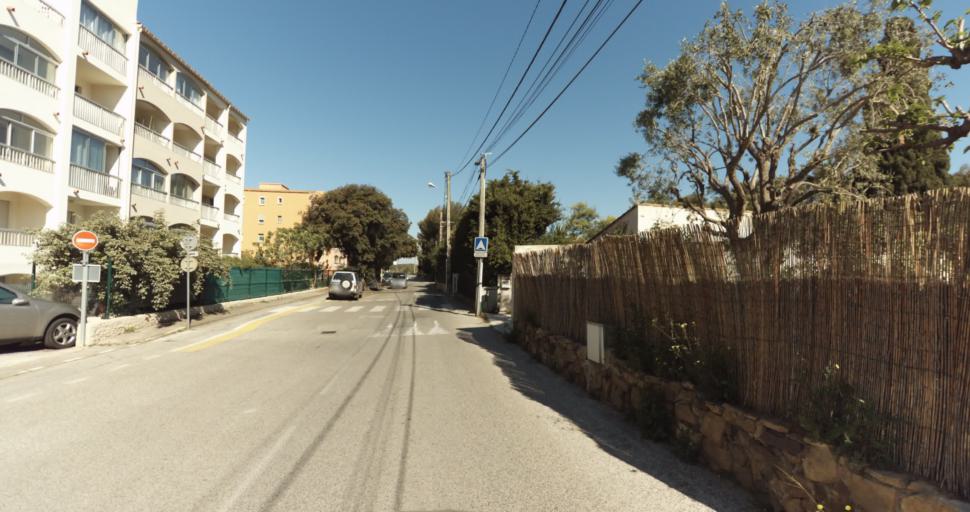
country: FR
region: Provence-Alpes-Cote d'Azur
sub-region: Departement du Var
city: Saint-Mandrier-sur-Mer
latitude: 43.0734
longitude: 5.9124
